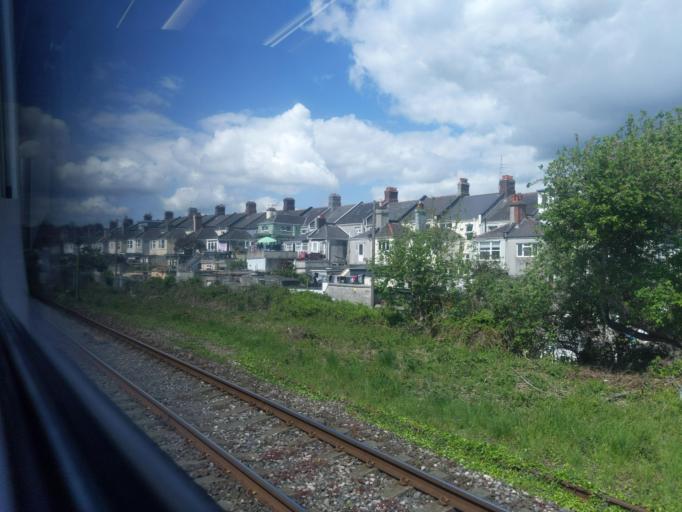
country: GB
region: England
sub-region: Plymouth
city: Plymouth
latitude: 50.3775
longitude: -4.1512
